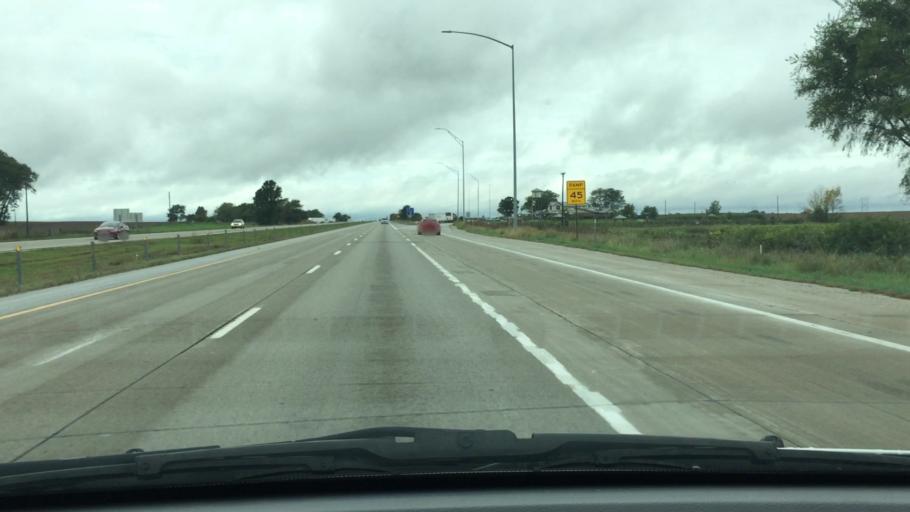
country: US
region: Iowa
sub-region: Polk County
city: Mitchellville
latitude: 41.6806
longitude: -93.3854
